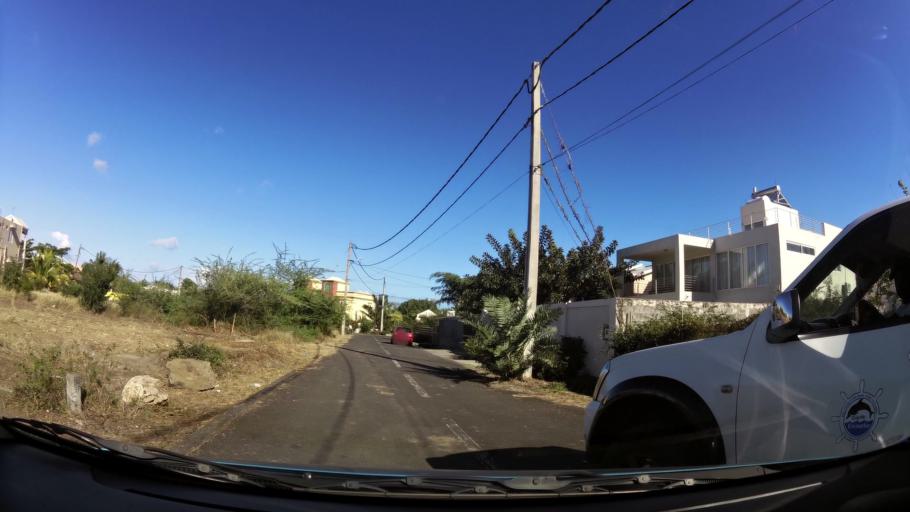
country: MU
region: Black River
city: Grande Riviere Noire
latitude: -20.3547
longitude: 57.3651
